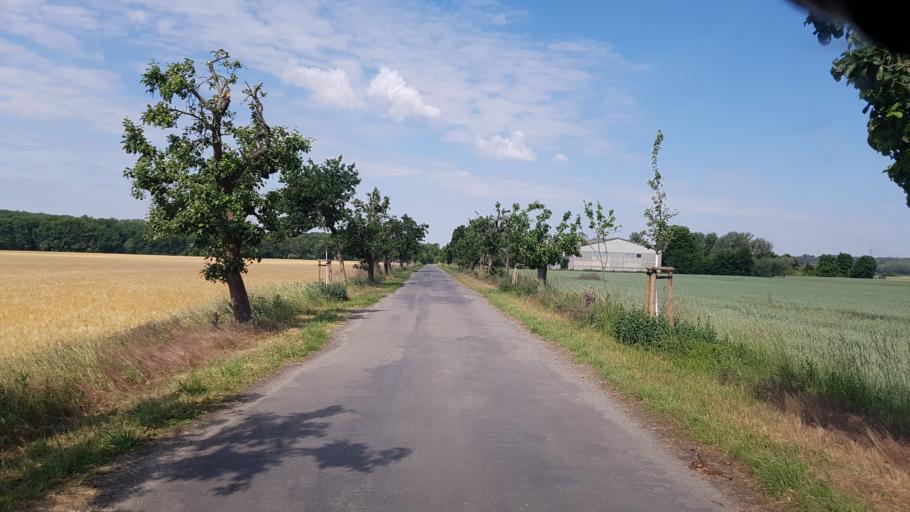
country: DE
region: Brandenburg
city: Doberlug-Kirchhain
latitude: 51.6240
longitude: 13.5523
